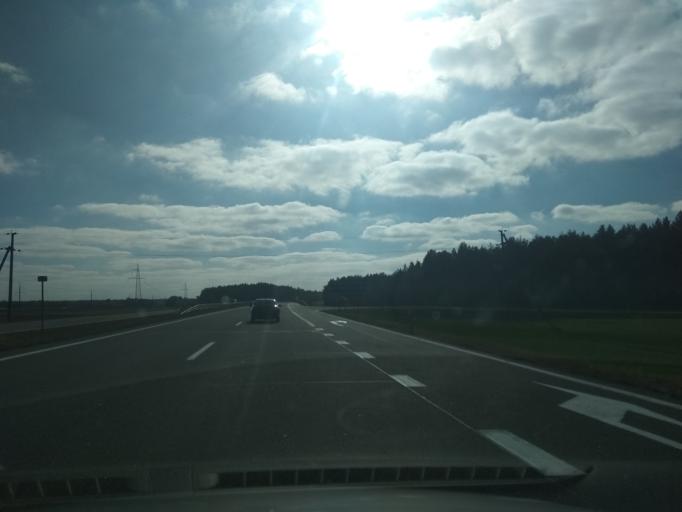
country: BY
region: Brest
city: Baranovichi
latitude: 53.0893
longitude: 25.8870
